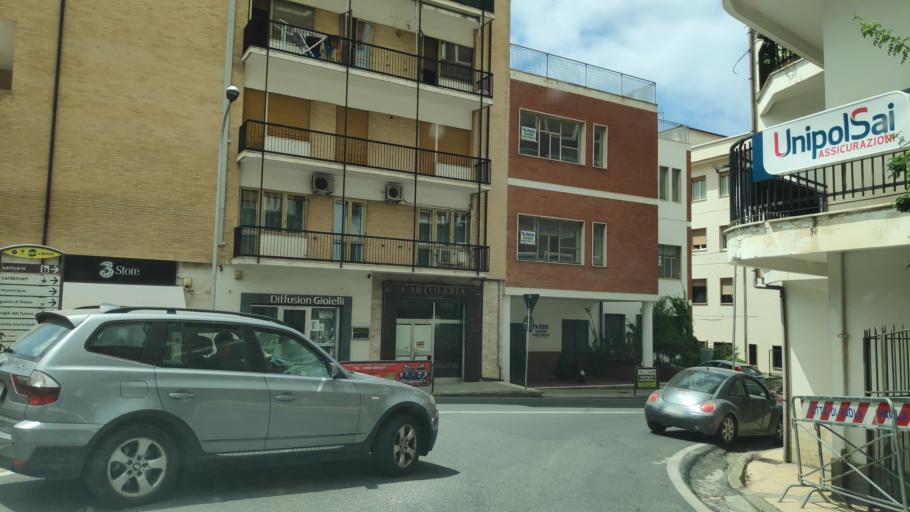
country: IT
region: Calabria
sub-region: Provincia di Cosenza
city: Paola
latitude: 39.3575
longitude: 16.0420
